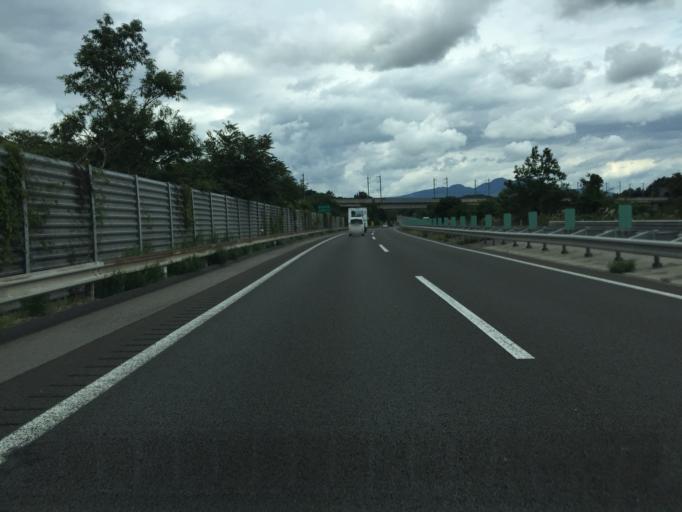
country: JP
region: Miyagi
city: Shiroishi
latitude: 37.9694
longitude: 140.6150
